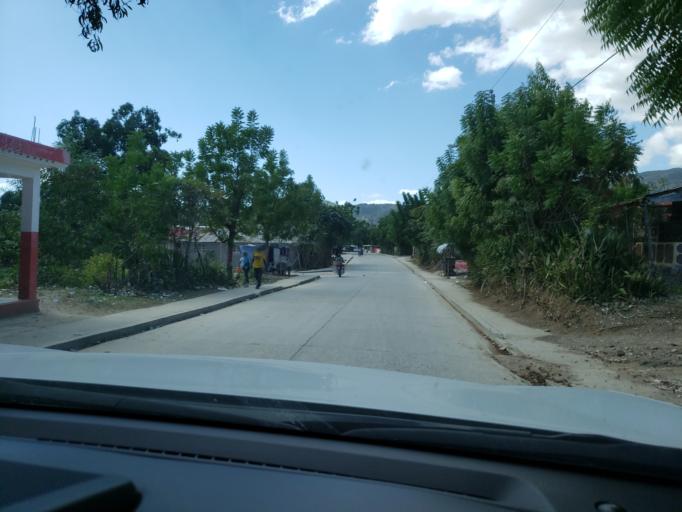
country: HT
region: Grandans
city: Anse-a-Veau
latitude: 18.4506
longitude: -73.3822
